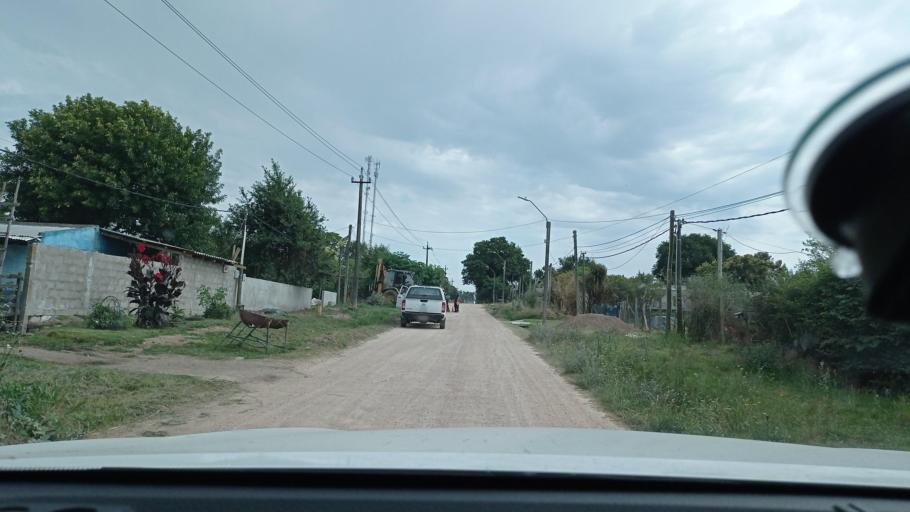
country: UY
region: Canelones
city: Pando
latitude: -34.7092
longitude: -55.9689
